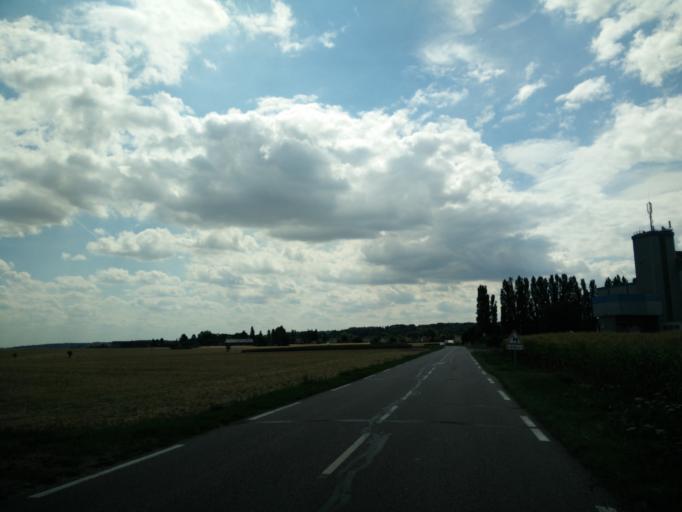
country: FR
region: Ile-de-France
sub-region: Departement des Yvelines
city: Guerville
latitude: 48.8991
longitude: 1.7369
